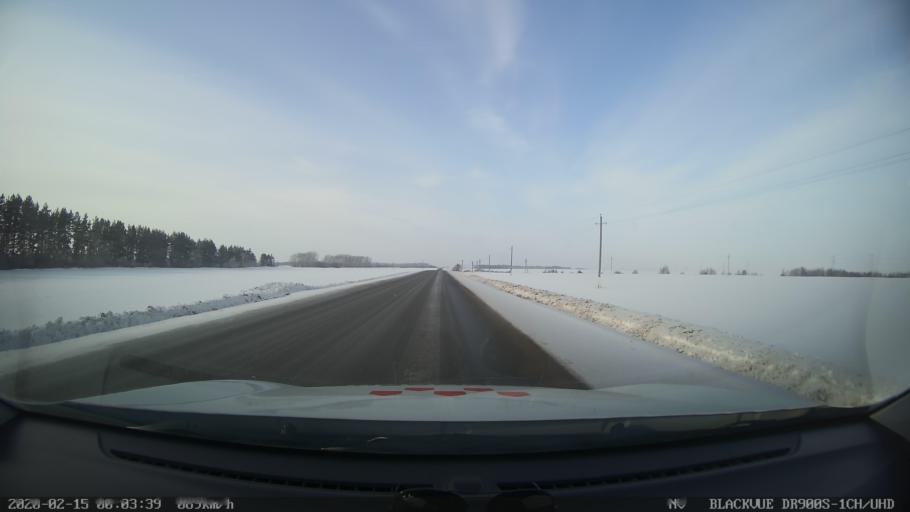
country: RU
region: Tatarstan
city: Kuybyshevskiy Zaton
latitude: 55.3739
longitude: 48.9947
